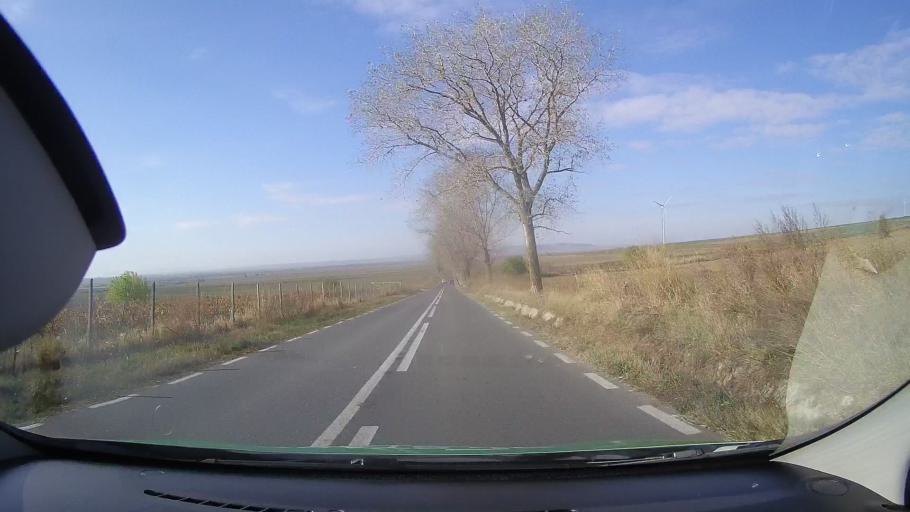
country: RO
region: Tulcea
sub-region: Comuna Valea Nucarilor
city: Iazurile
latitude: 45.0245
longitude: 28.9773
